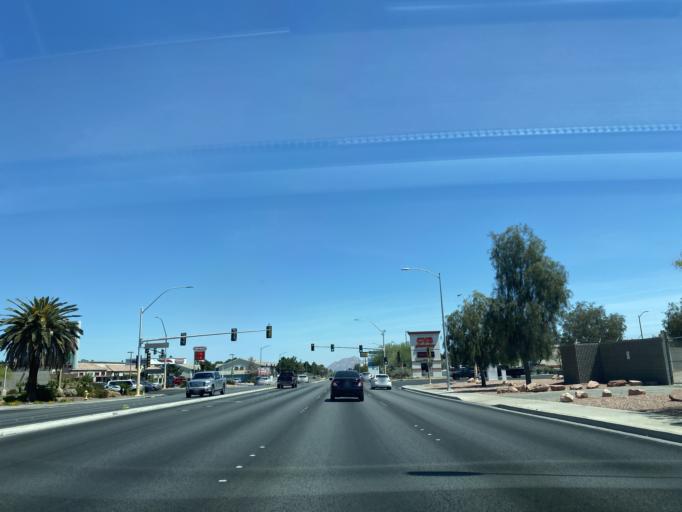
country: US
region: Nevada
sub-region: Clark County
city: Spring Valley
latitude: 36.1958
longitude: -115.2342
